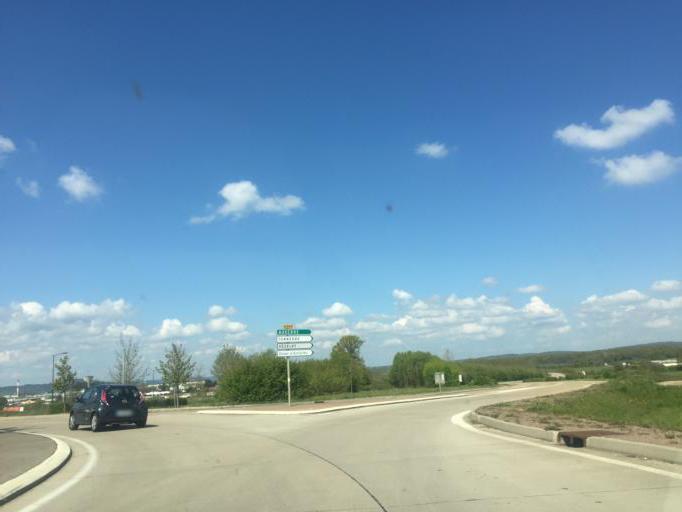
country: FR
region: Bourgogne
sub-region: Departement de l'Yonne
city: Avallon
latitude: 47.4945
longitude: 3.9373
